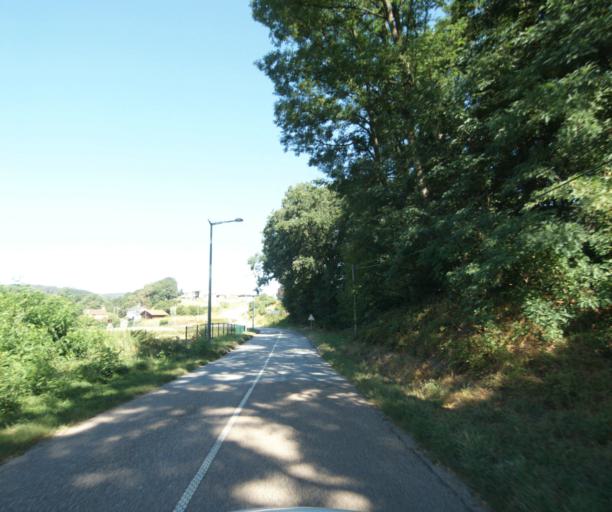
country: FR
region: Lorraine
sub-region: Departement des Vosges
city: Chantraine
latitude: 48.1507
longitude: 6.4642
